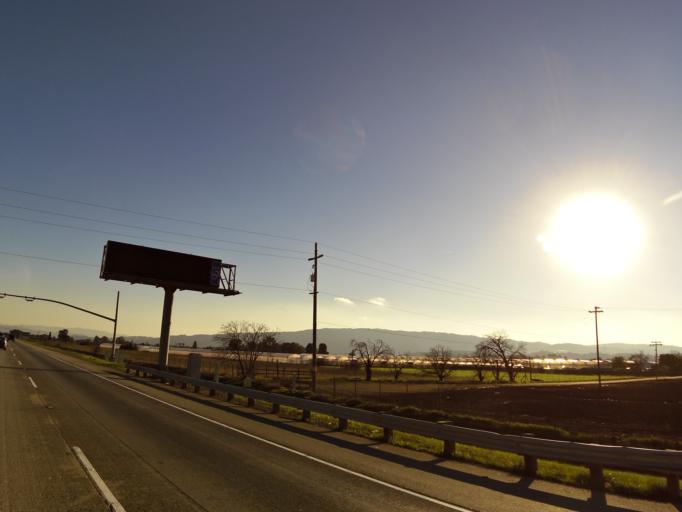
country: US
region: California
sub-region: Santa Clara County
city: San Martin
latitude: 37.0539
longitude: -121.5824
